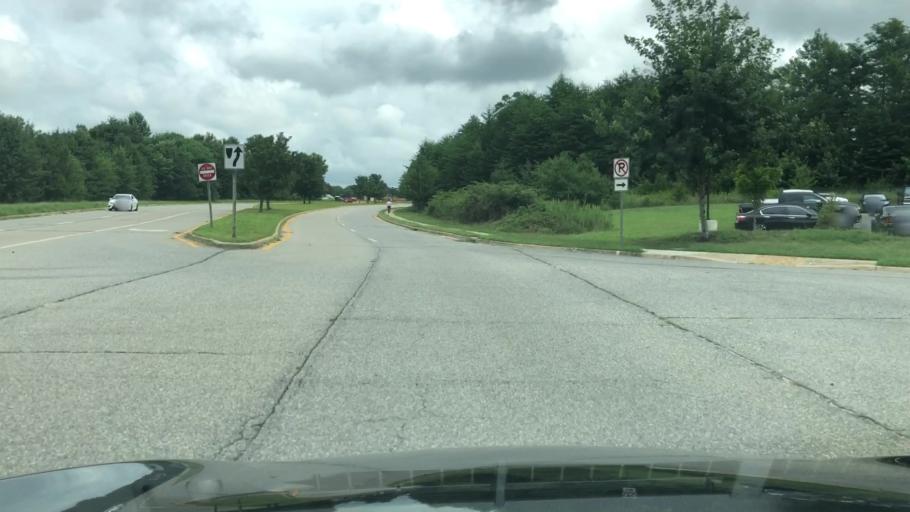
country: US
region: Virginia
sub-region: Stafford County
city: Falmouth
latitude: 38.3631
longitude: -77.5269
